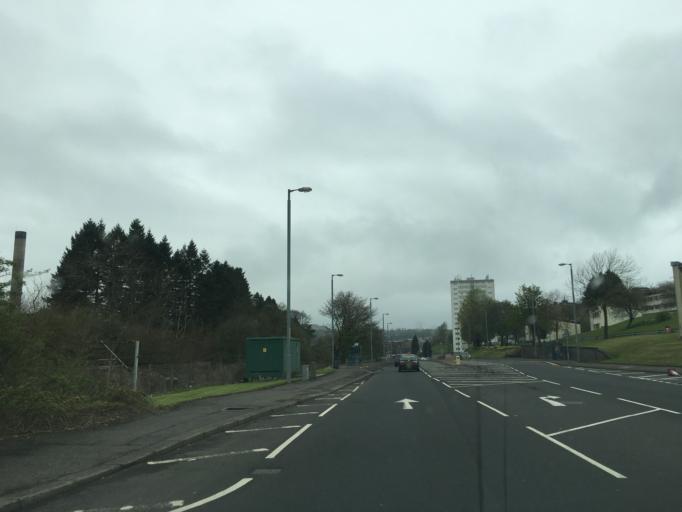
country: GB
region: Scotland
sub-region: Inverclyde
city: Gourock
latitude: 55.9406
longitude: -4.7957
